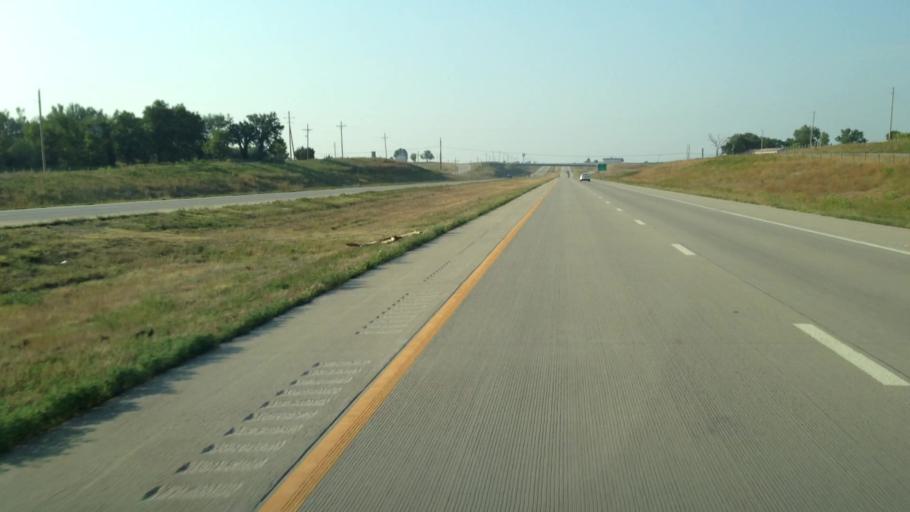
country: US
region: Kansas
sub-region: Douglas County
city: Baldwin City
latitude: 38.8090
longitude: -95.2689
